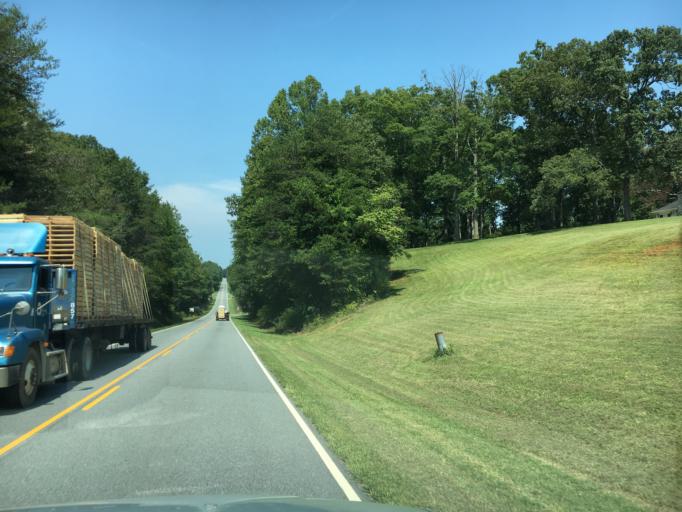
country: US
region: North Carolina
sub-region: Rutherford County
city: Rutherfordton
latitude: 35.3879
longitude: -81.9590
